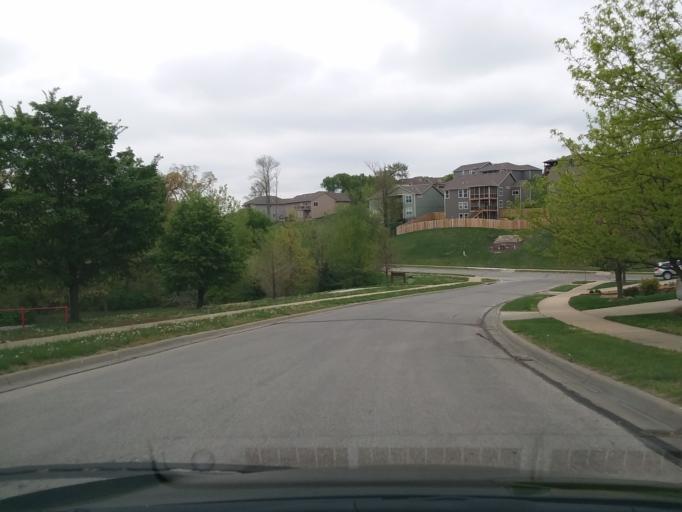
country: US
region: Kansas
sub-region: Douglas County
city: Lawrence
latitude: 38.9936
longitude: -95.2873
